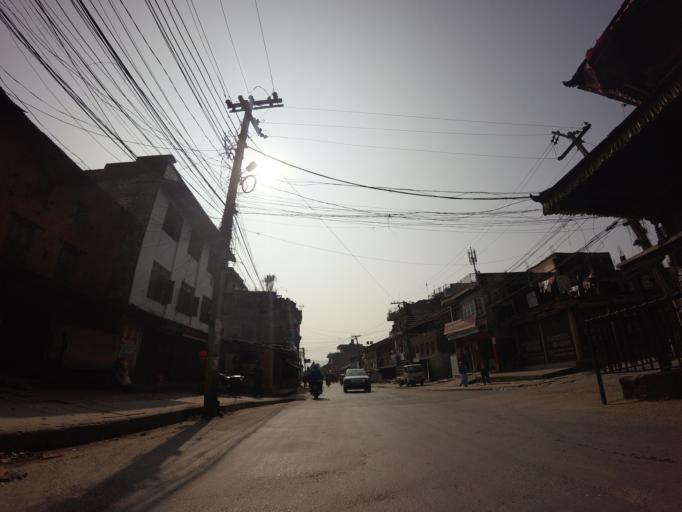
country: NP
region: Western Region
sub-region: Gandaki Zone
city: Pokhara
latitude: 28.2307
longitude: 83.9849
